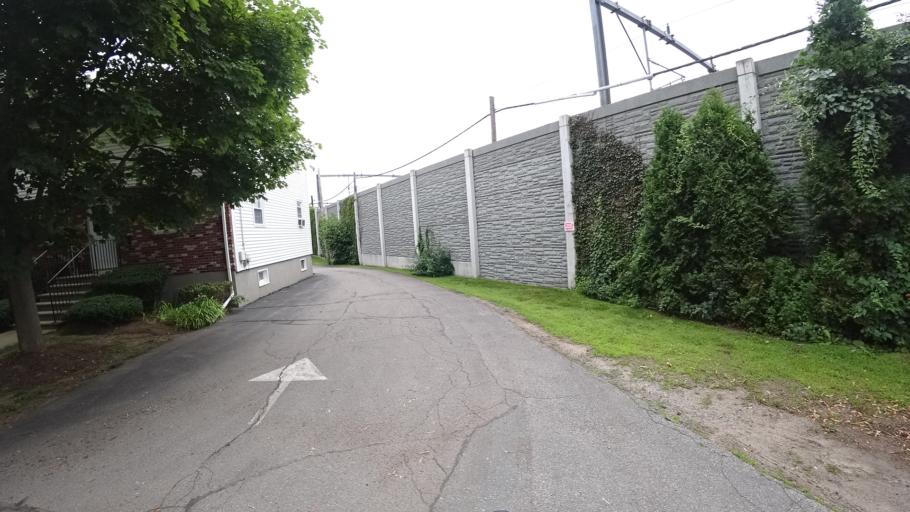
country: US
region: Massachusetts
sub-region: Norfolk County
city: Dedham
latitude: 42.2297
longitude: -71.1381
